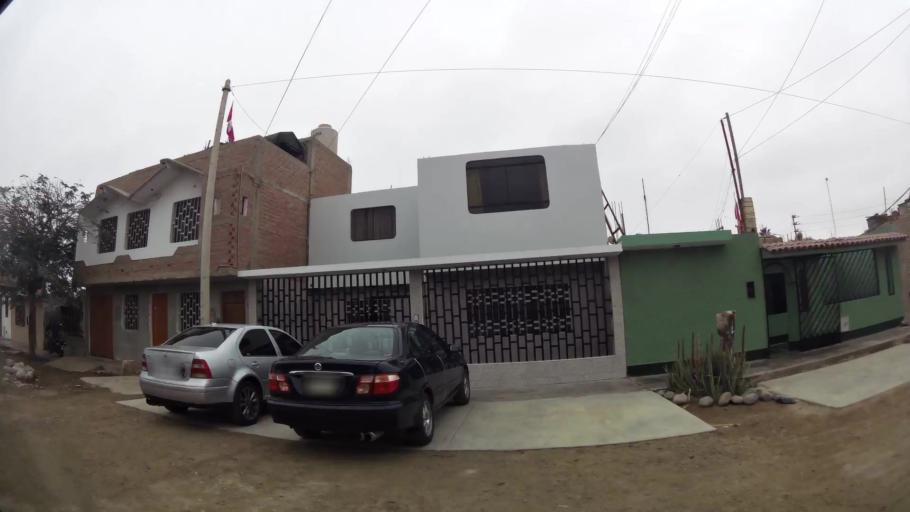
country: PE
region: Ica
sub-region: Provincia de Pisco
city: Pisco
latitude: -13.7110
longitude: -76.2117
